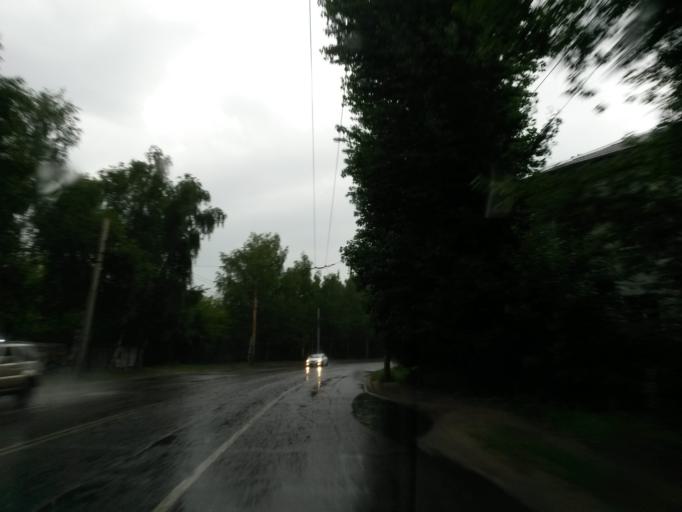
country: RU
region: Jaroslavl
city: Yaroslavl
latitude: 57.6611
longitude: 39.8570
